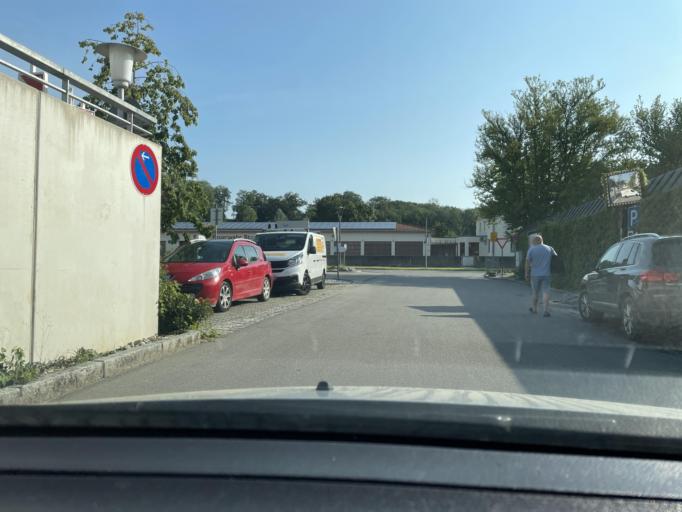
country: DE
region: Bavaria
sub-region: Upper Bavaria
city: Muehldorf
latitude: 48.2427
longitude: 12.5308
